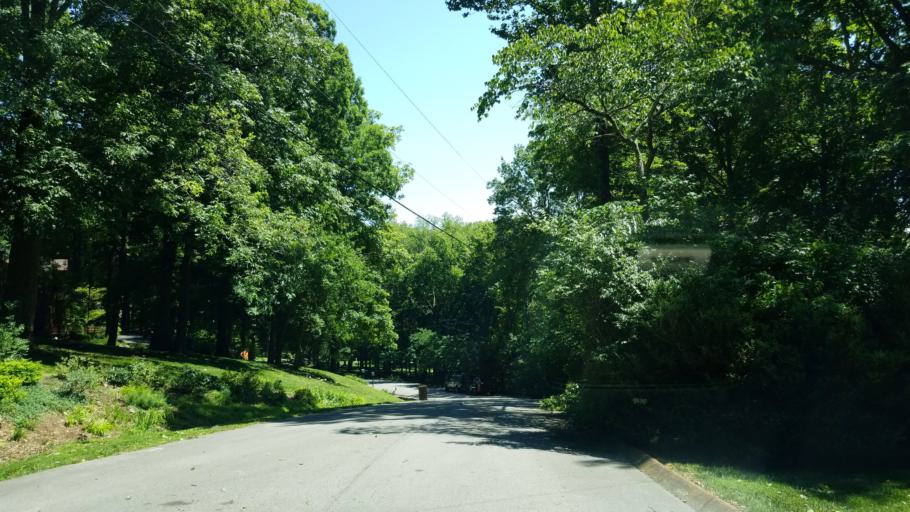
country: US
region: Tennessee
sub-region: Davidson County
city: Forest Hills
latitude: 36.0584
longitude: -86.8103
